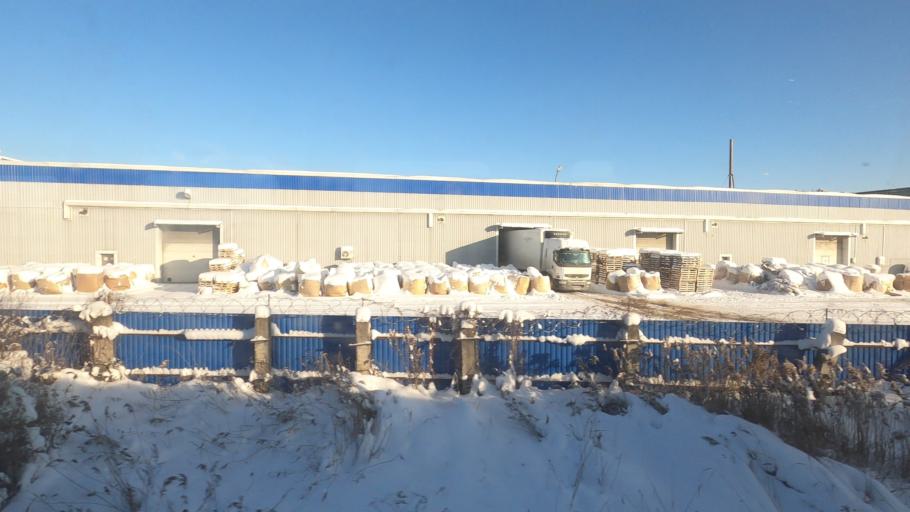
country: RU
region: Moskovskaya
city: Dmitrov
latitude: 56.3764
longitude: 37.5216
